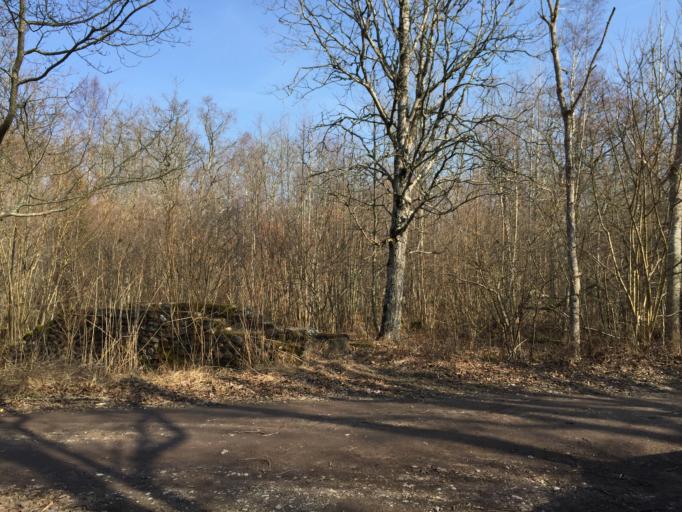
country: LV
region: Dundaga
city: Dundaga
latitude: 57.9319
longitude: 22.0201
